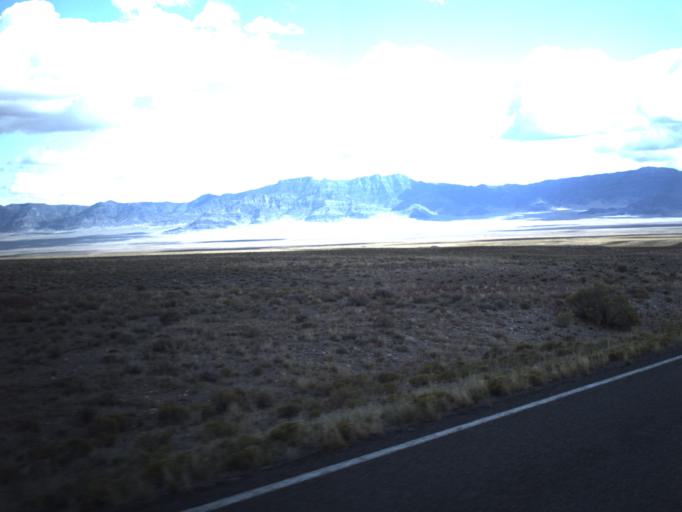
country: US
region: Utah
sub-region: Beaver County
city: Milford
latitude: 38.5694
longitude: -113.7824
